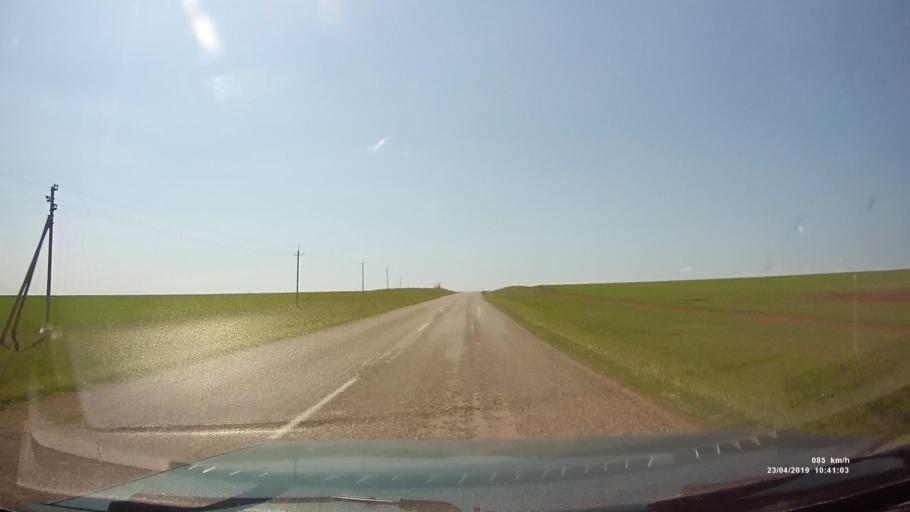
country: RU
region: Kalmykiya
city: Yashalta
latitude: 46.4981
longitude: 42.6383
